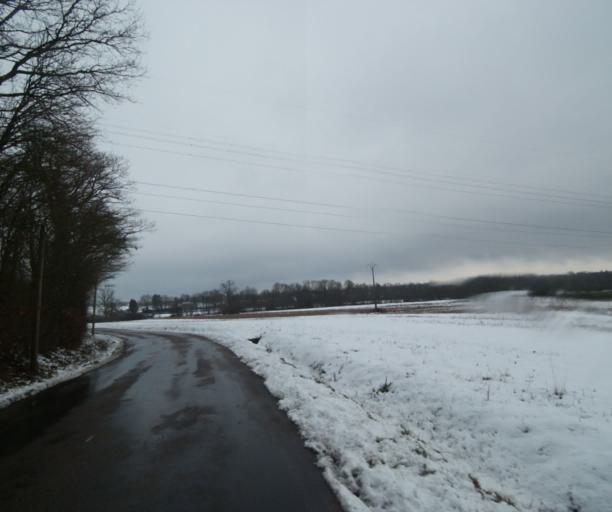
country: FR
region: Champagne-Ardenne
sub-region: Departement de la Haute-Marne
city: Laneuville-a-Remy
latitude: 48.5130
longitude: 4.8455
